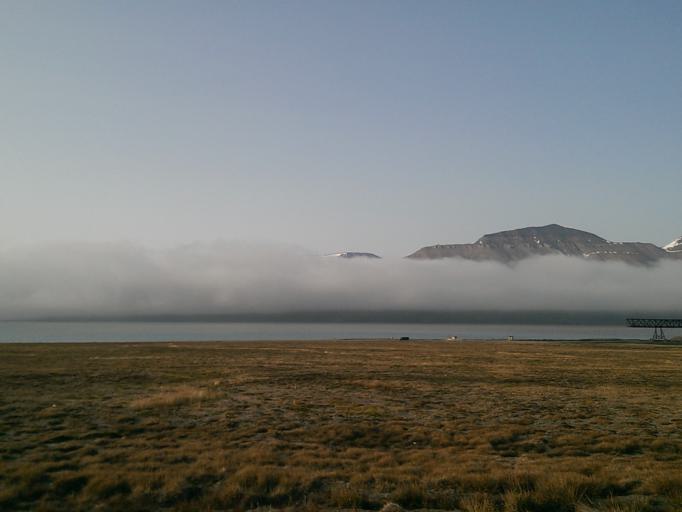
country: SJ
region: Svalbard
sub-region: Spitsbergen
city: Longyearbyen
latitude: 78.2447
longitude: 15.5181
